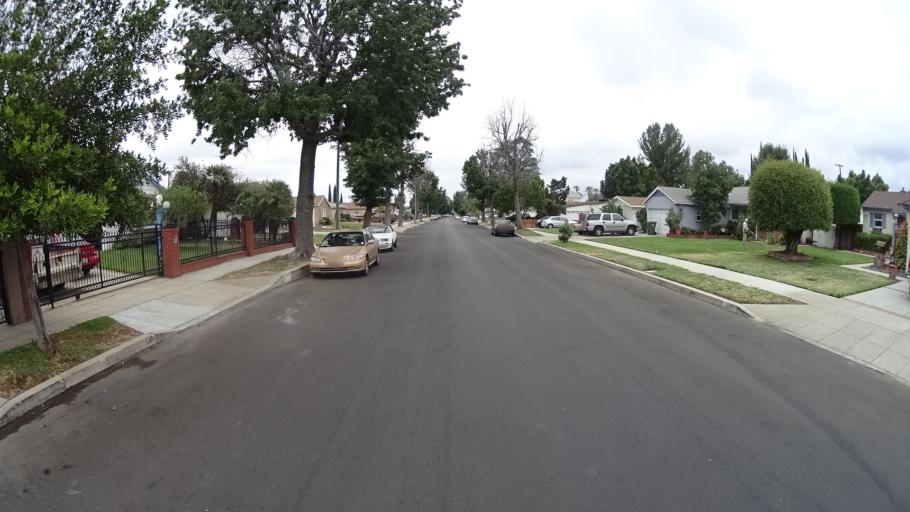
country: US
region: California
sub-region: Los Angeles County
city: San Fernando
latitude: 34.2421
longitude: -118.4571
